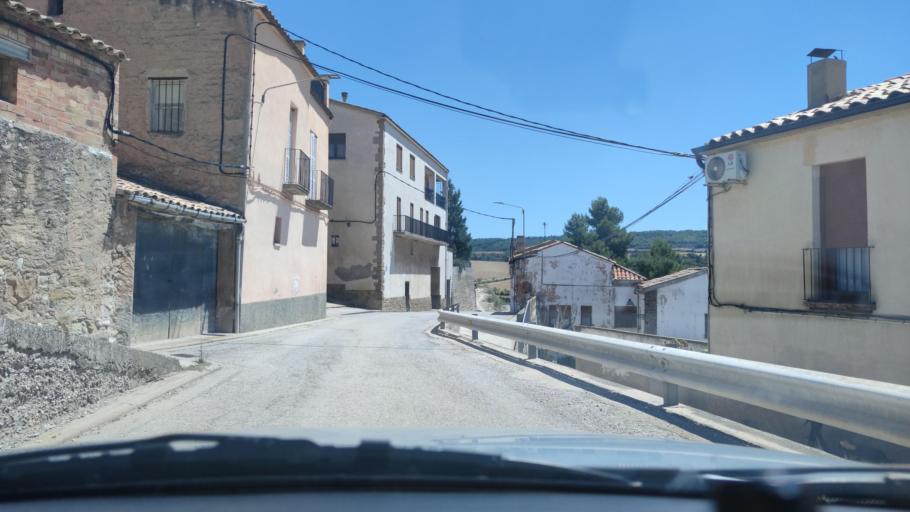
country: ES
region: Catalonia
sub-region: Provincia de Lleida
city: Ivorra
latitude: 41.7722
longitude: 1.3943
